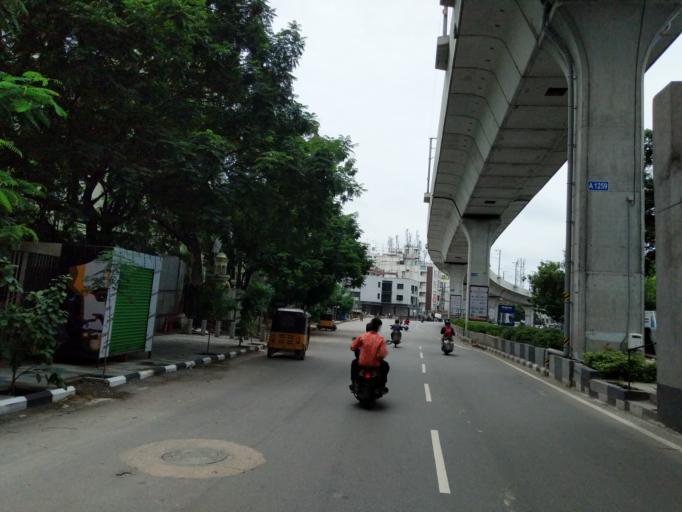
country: IN
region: Telangana
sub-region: Hyderabad
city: Hyderabad
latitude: 17.3973
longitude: 78.4710
